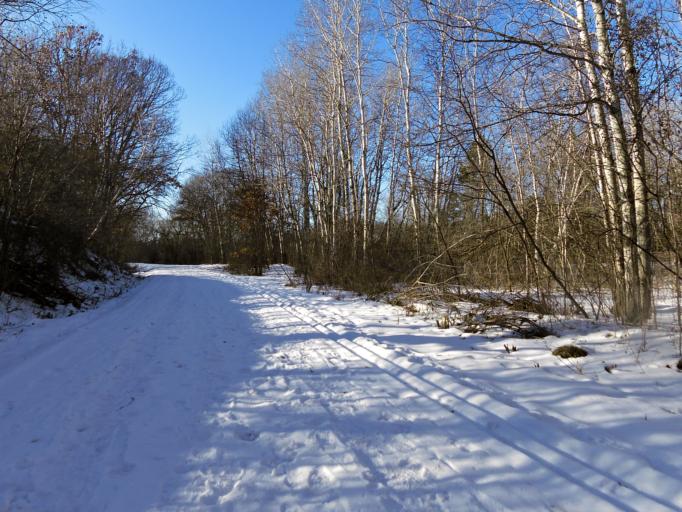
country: US
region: Minnesota
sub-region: Washington County
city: Grant
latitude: 45.0787
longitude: -92.8811
